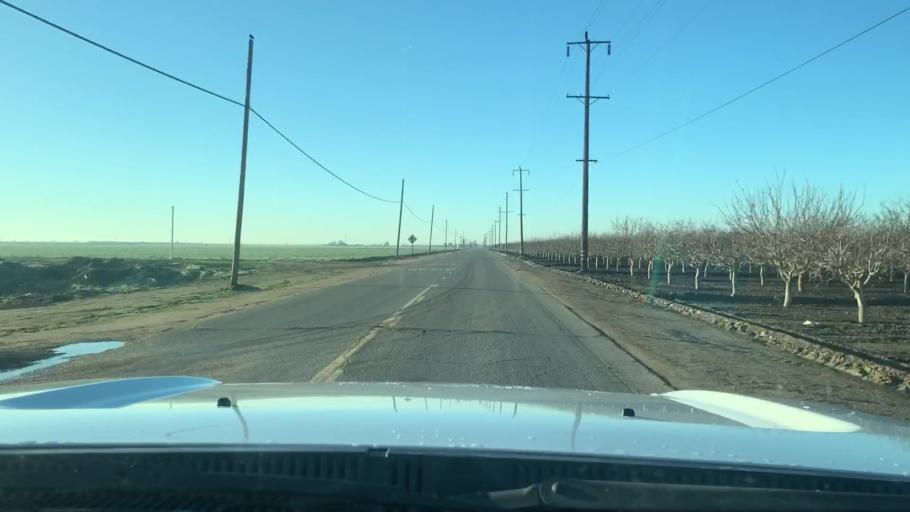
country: US
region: California
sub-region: Tulare County
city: Tulare
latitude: 36.2028
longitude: -119.4212
